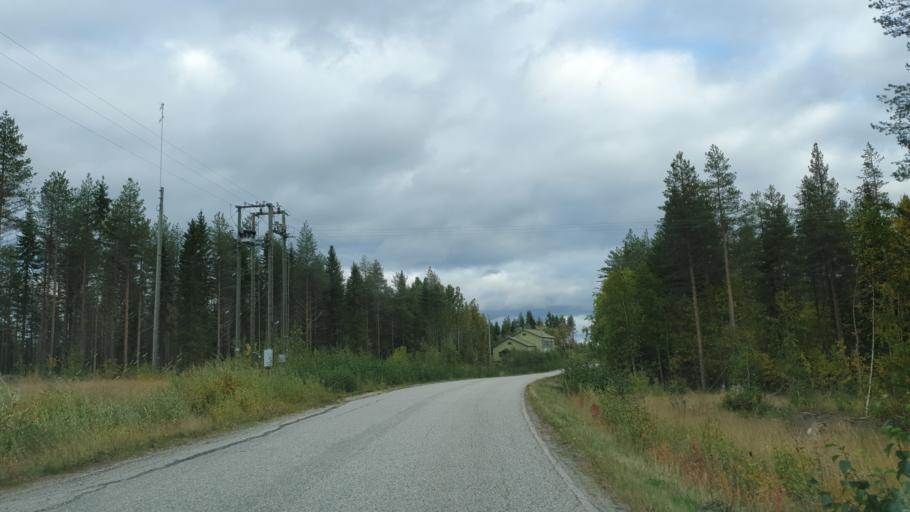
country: FI
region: Kainuu
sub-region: Kehys-Kainuu
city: Kuhmo
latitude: 63.9551
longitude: 29.7304
